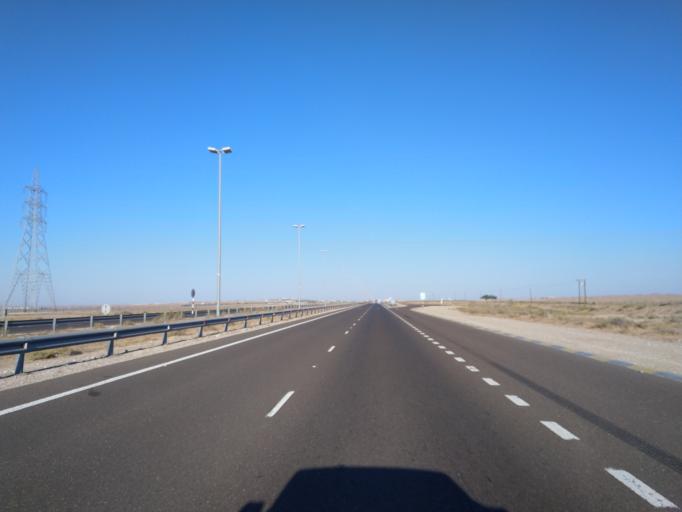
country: OM
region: Al Buraimi
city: Al Buraymi
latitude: 24.4961
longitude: 55.4270
